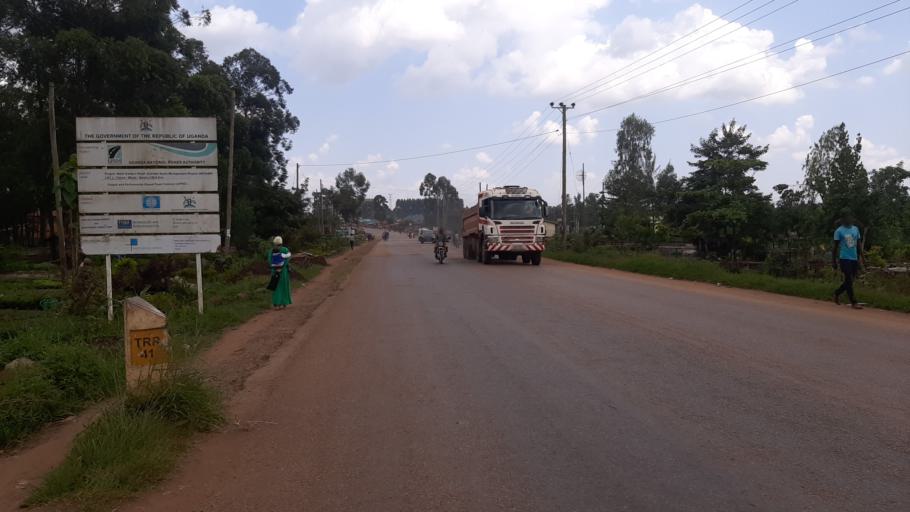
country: UG
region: Eastern Region
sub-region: Mbale District
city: Mbale
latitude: 1.0524
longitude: 34.1785
